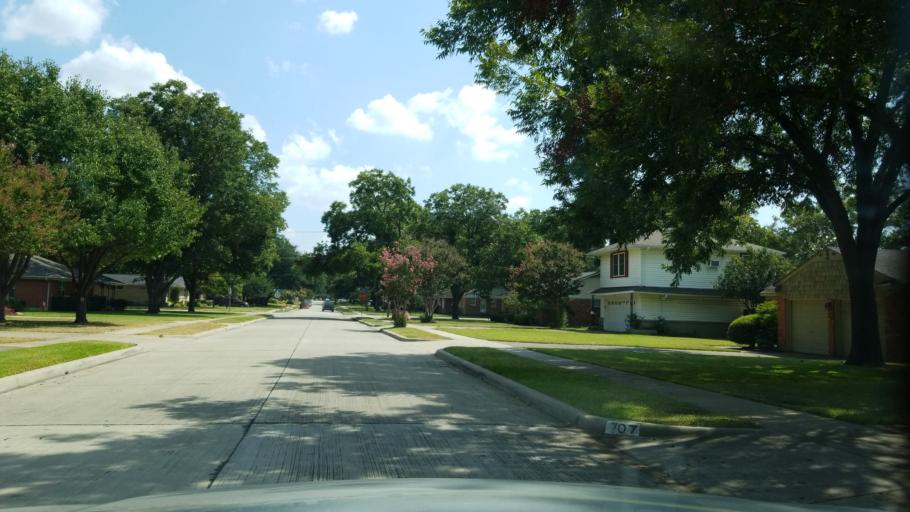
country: US
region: Texas
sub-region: Dallas County
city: Richardson
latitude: 32.9528
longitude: -96.7448
